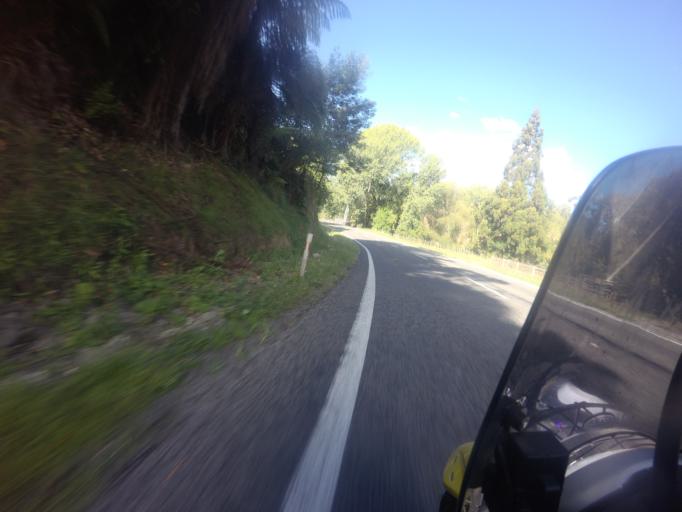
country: NZ
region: Bay of Plenty
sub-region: Whakatane District
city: Whakatane
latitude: -38.0200
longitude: 177.0800
